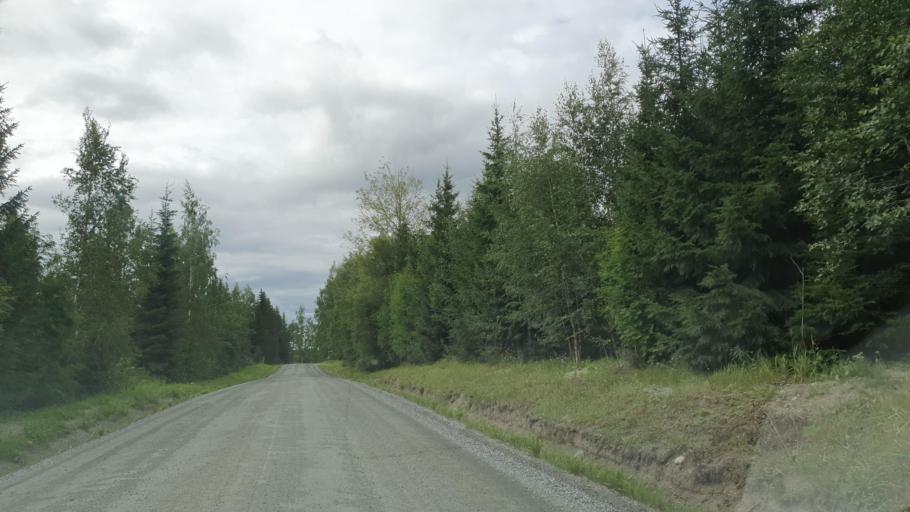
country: FI
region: Northern Savo
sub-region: Ylae-Savo
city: Iisalmi
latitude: 63.5174
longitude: 27.1055
